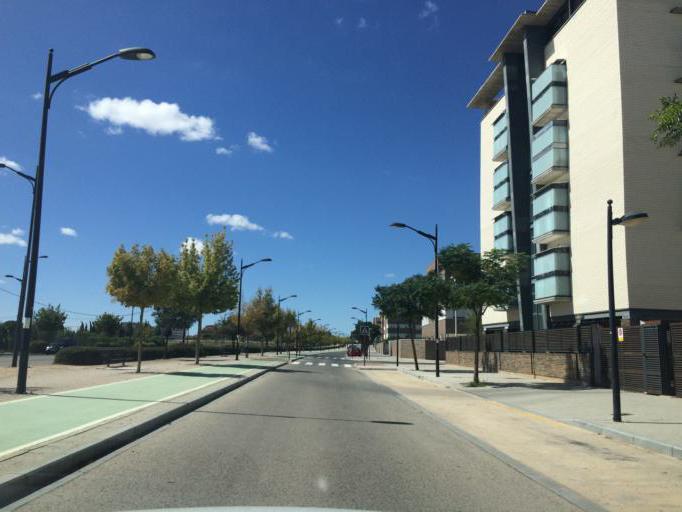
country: ES
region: Castille-La Mancha
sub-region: Provincia de Albacete
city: Albacete
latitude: 38.9779
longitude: -1.8402
